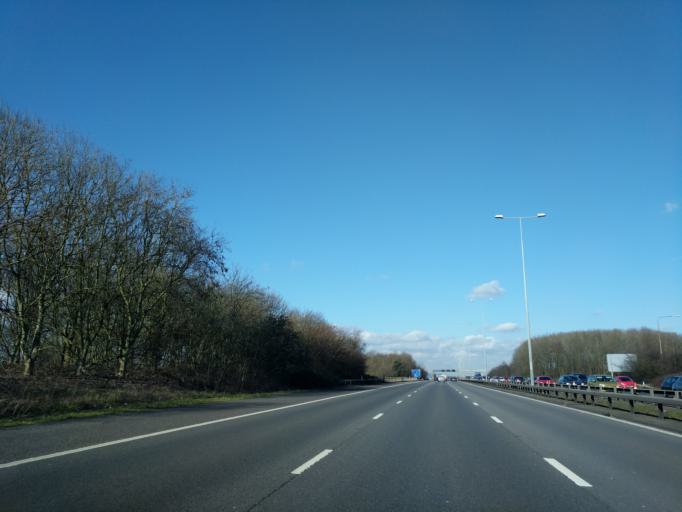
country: GB
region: England
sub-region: Surrey
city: Chertsey
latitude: 51.3979
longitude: -0.5360
